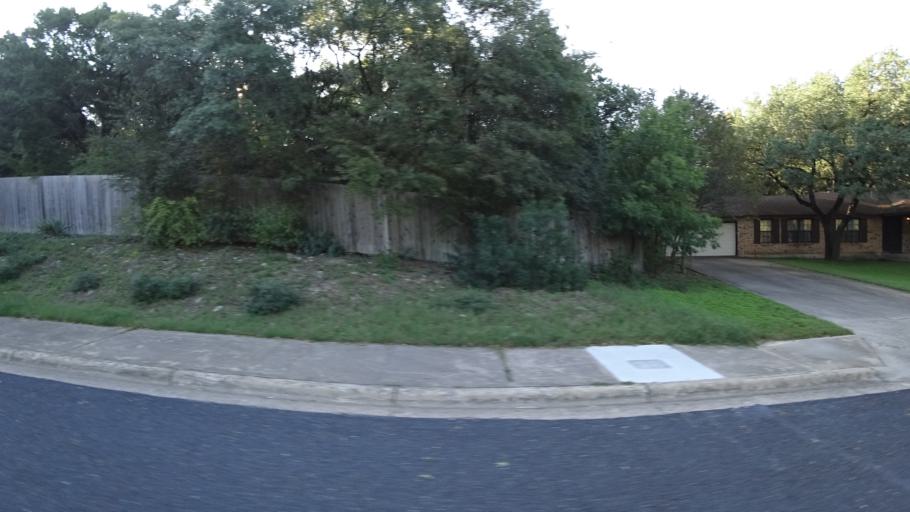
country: US
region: Texas
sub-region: Travis County
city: Rollingwood
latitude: 30.2643
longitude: -97.8005
